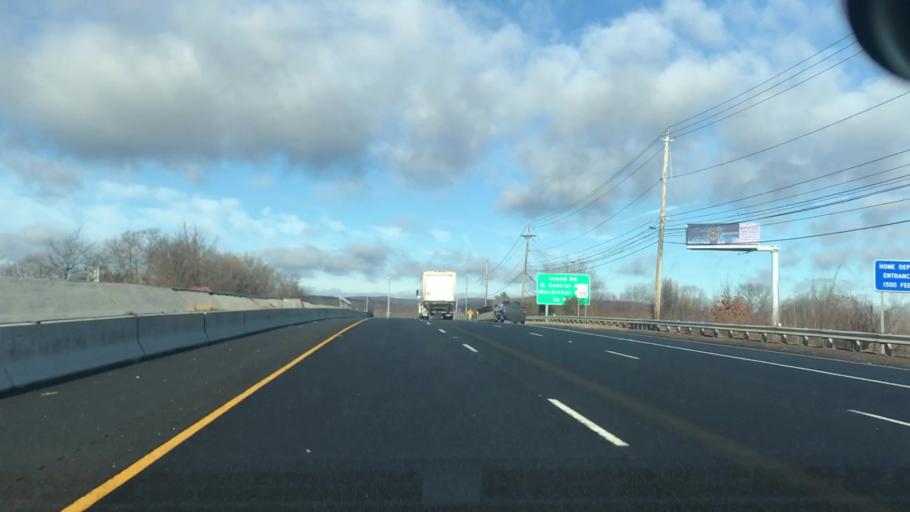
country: US
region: New Jersey
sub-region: Bergen County
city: Mahwah
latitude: 41.0749
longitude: -74.1446
